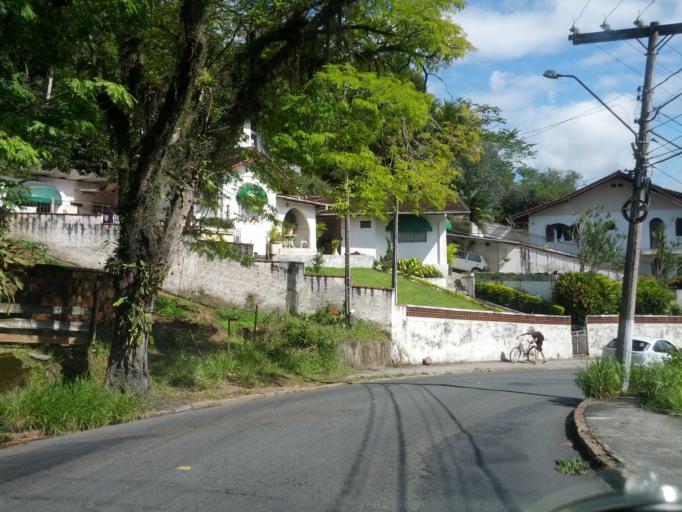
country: BR
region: Santa Catarina
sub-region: Blumenau
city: Blumenau
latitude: -26.9203
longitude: -49.0876
